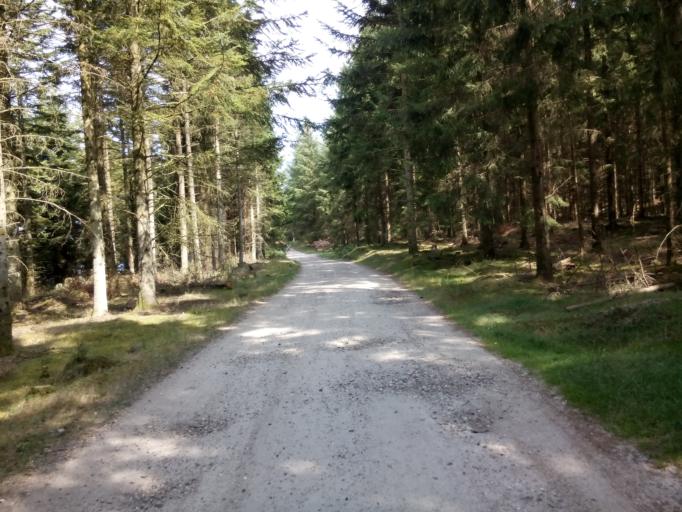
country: DK
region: Central Jutland
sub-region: Skanderborg Kommune
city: Ry
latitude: 56.0905
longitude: 9.7386
